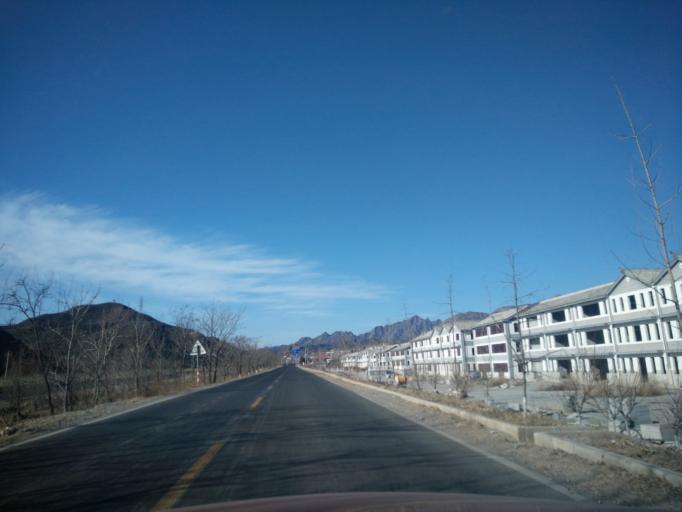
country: CN
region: Beijing
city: Zhaitang
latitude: 39.9790
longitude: 115.7152
